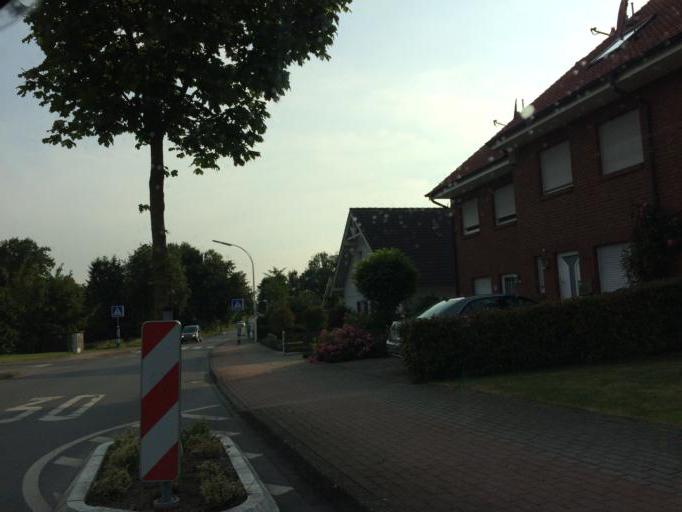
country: DE
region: North Rhine-Westphalia
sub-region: Regierungsbezirk Munster
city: Nottuln
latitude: 51.9244
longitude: 7.3631
